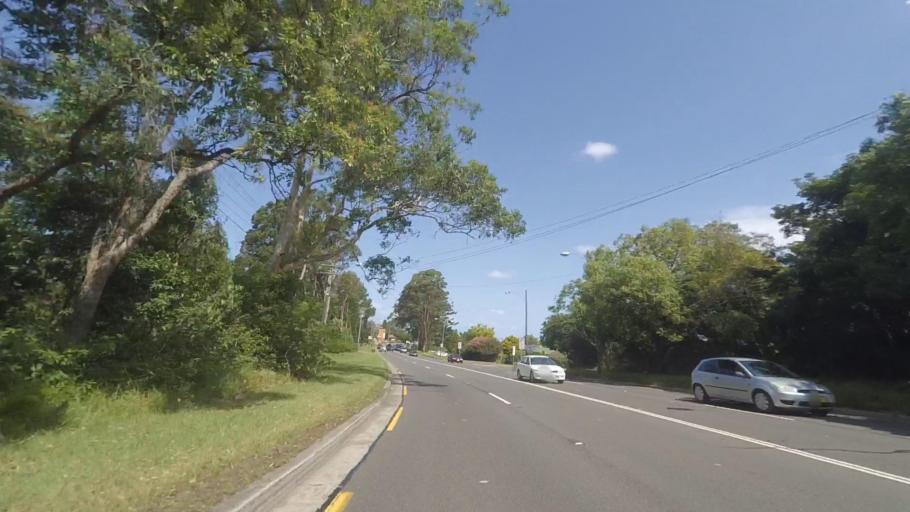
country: AU
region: New South Wales
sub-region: Parramatta
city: Carlingford
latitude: -33.7687
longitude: 151.0487
